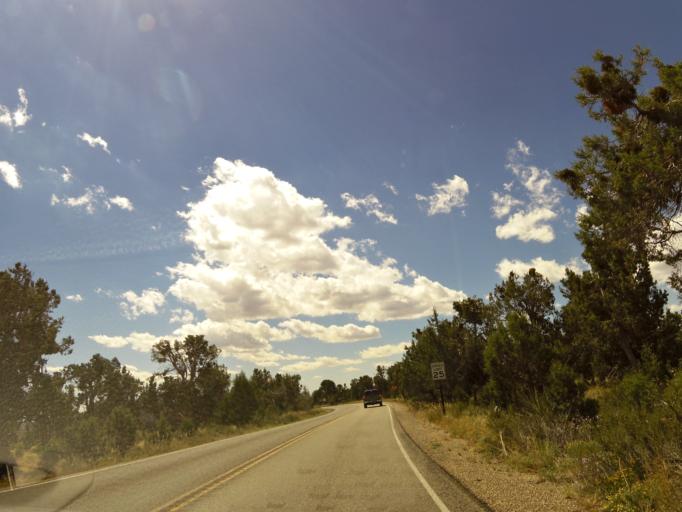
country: US
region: Colorado
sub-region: Montezuma County
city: Cortez
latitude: 37.1917
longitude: -108.4850
